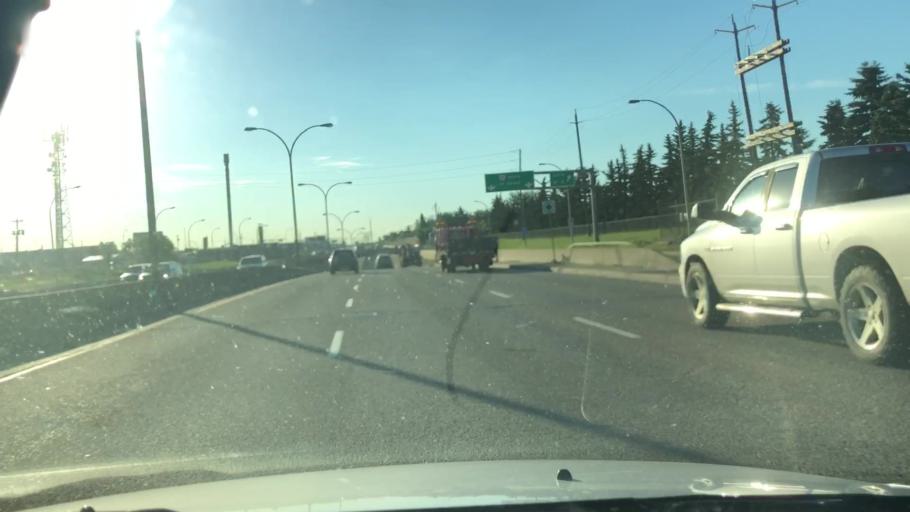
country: CA
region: Alberta
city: Edmonton
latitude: 53.5814
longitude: -113.4964
